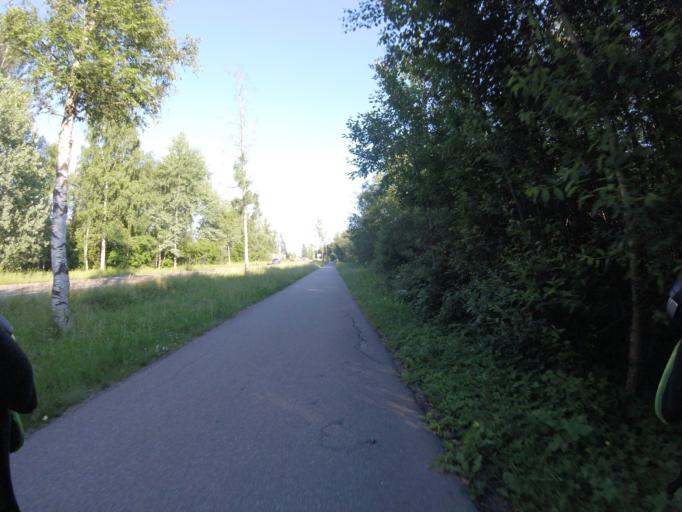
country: NO
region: Akershus
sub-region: Skedsmo
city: Lillestrom
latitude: 59.9647
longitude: 11.0566
